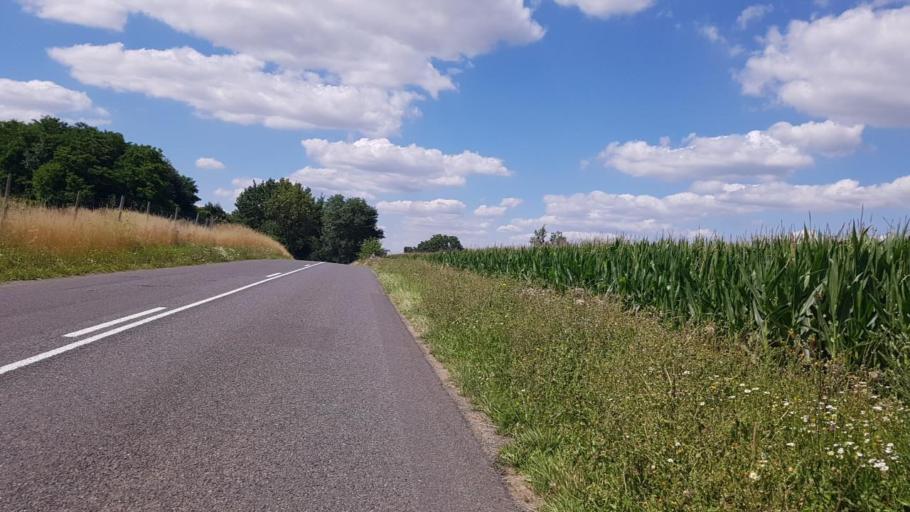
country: FR
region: Ile-de-France
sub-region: Departement de Seine-et-Marne
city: Moussy-le-Vieux
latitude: 49.0266
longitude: 2.6419
